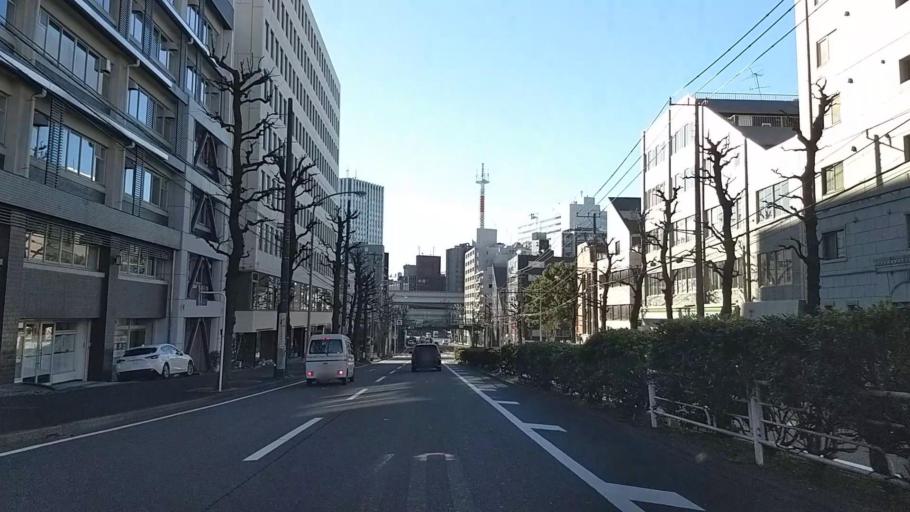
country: JP
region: Kanagawa
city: Yokohama
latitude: 35.4715
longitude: 139.6187
